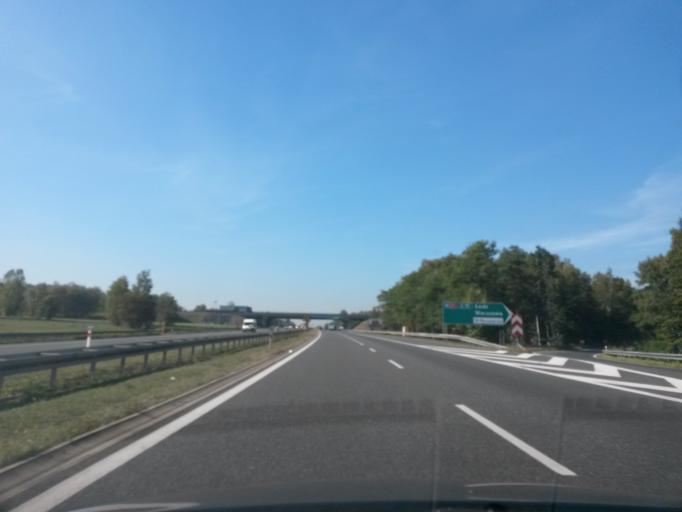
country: PL
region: Silesian Voivodeship
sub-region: Myslowice
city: Myslowice
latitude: 50.2070
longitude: 19.1704
